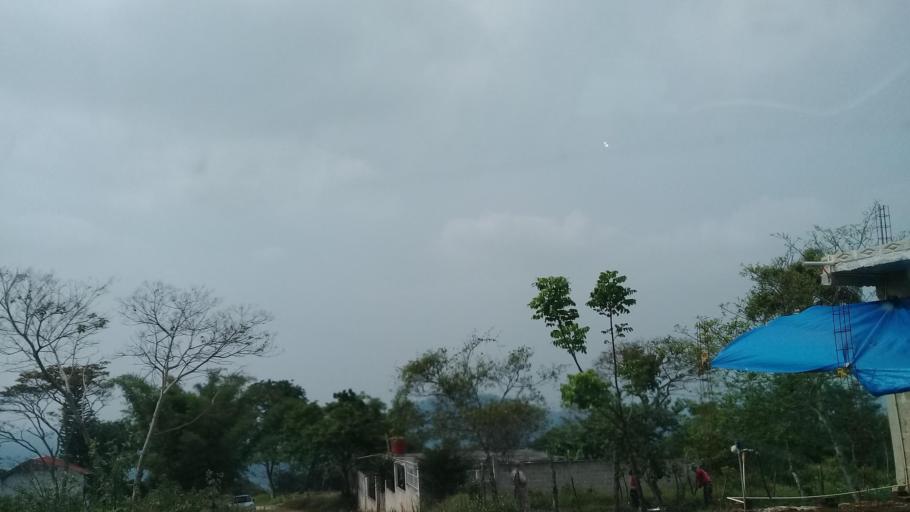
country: MX
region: Veracruz
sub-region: Xalapa
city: Fraccionamiento las Fuentes
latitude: 19.4906
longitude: -96.8983
